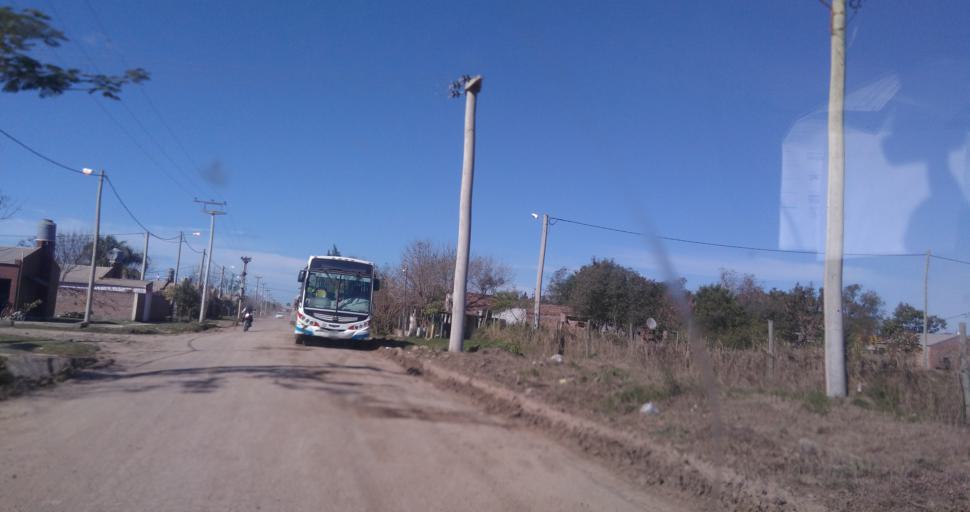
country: AR
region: Chaco
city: Fontana
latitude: -27.4556
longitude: -59.0470
